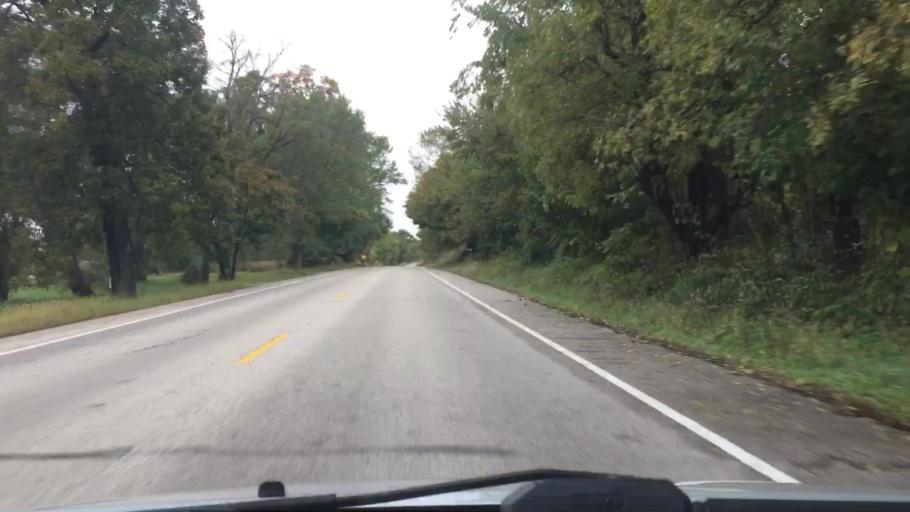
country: US
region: Wisconsin
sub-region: Waukesha County
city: Eagle
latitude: 42.8490
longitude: -88.5193
